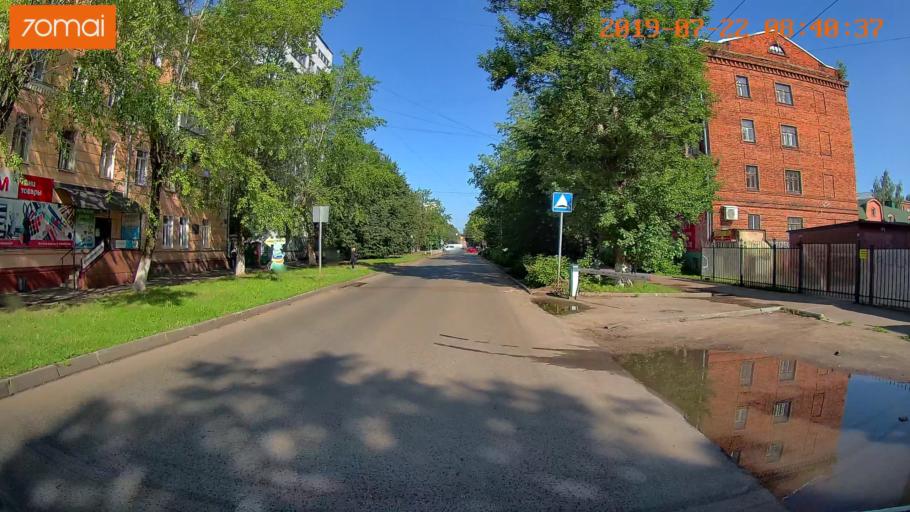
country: RU
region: Ivanovo
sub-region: Gorod Ivanovo
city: Ivanovo
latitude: 56.9984
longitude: 40.9868
